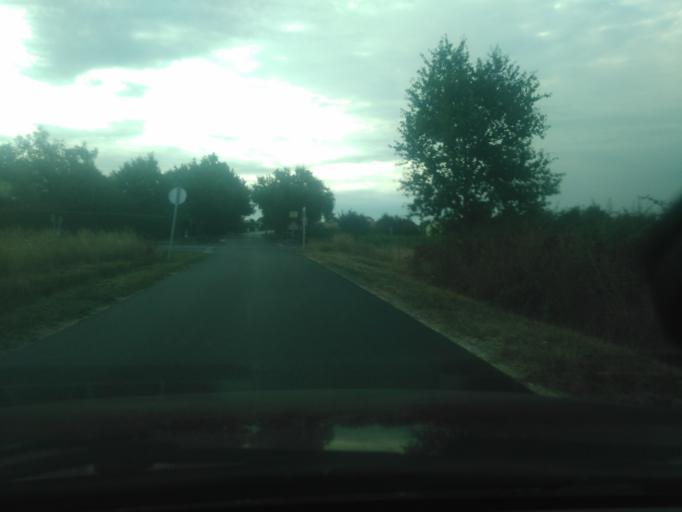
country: FR
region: Pays de la Loire
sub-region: Departement de la Vendee
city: Vendrennes
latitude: 46.7988
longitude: -1.1401
